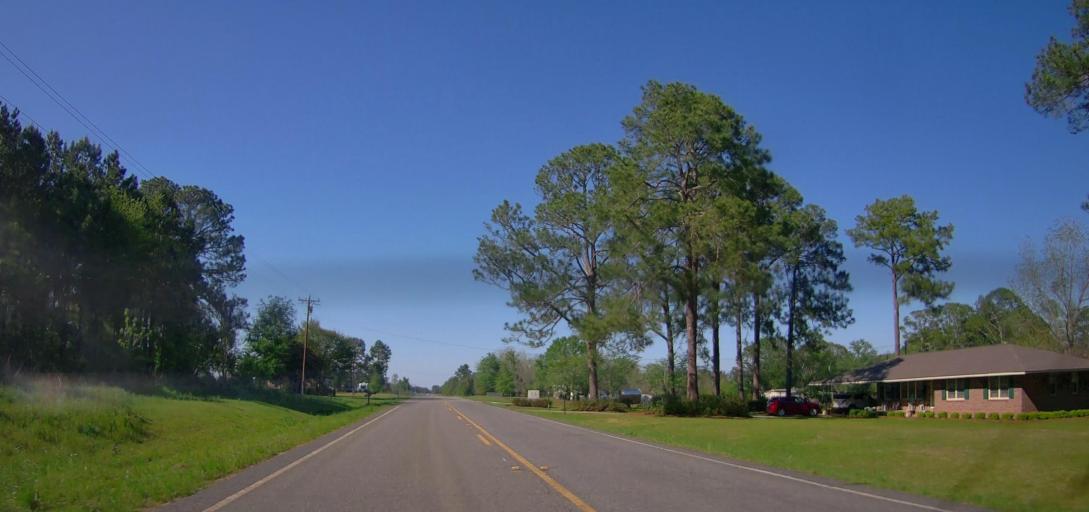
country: US
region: Georgia
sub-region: Wilcox County
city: Rochelle
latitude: 32.0641
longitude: -83.5036
